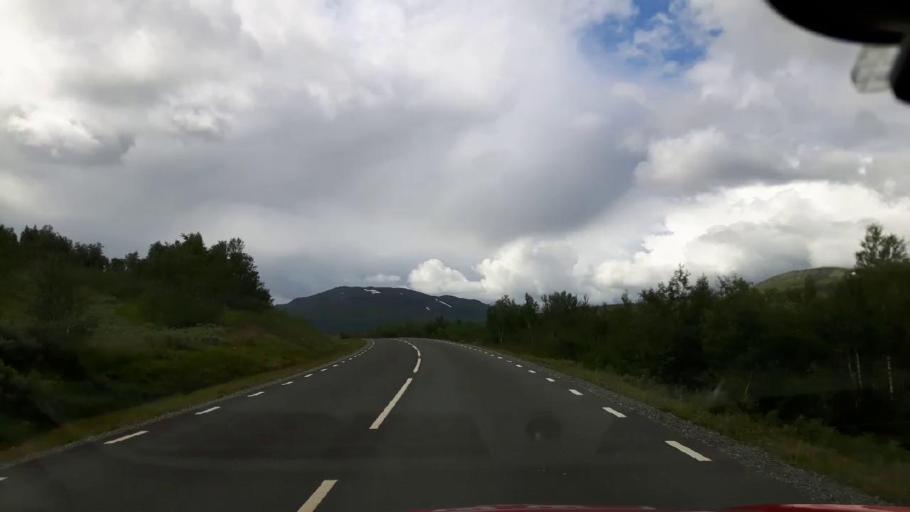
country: NO
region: Nordland
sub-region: Hattfjelldal
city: Hattfjelldal
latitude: 65.0057
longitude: 14.2595
